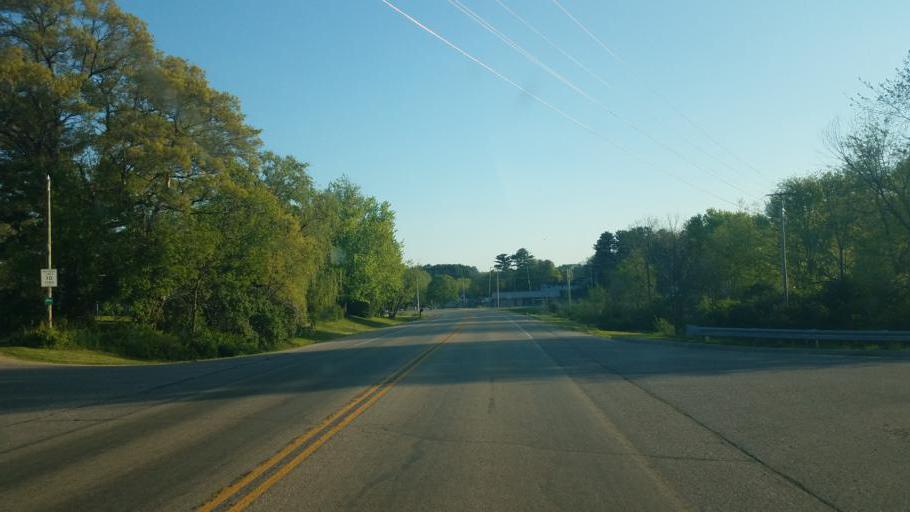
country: US
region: Wisconsin
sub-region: Sauk County
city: Reedsburg
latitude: 43.5861
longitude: -90.1280
